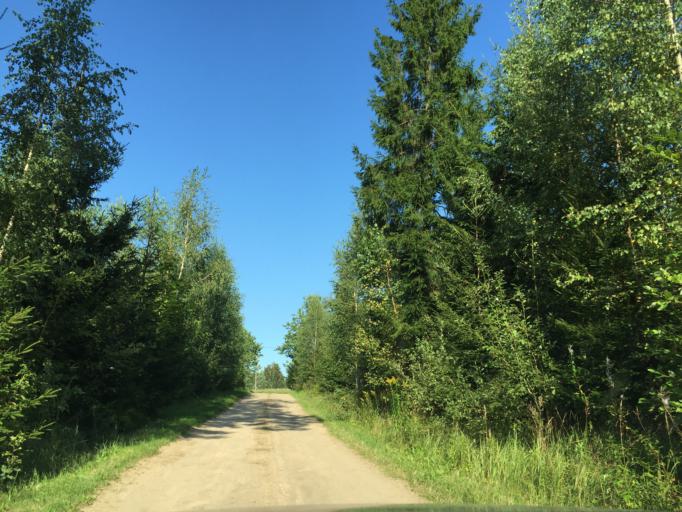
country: LV
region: Limbazu Rajons
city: Limbazi
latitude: 57.5593
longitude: 24.7853
